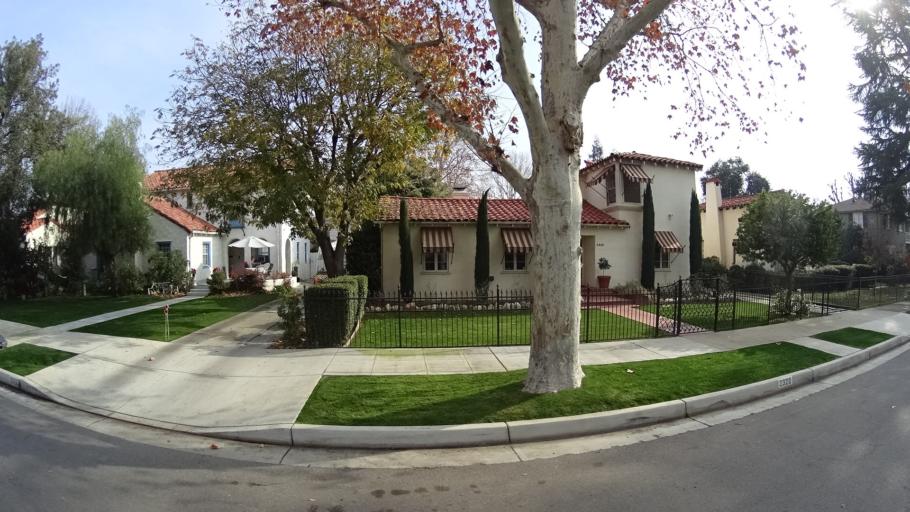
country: US
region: California
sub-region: Kern County
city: Bakersfield
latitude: 35.3805
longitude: -119.0304
